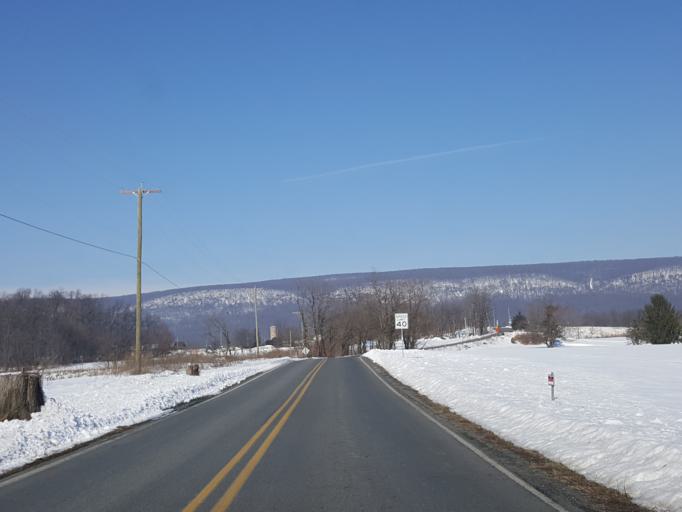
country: US
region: Pennsylvania
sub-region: Lebanon County
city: Myerstown
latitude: 40.4820
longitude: -76.2438
